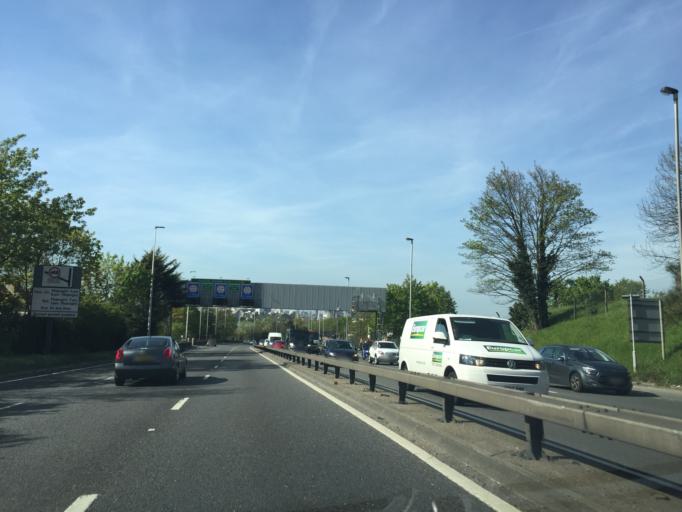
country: GB
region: England
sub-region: Greater London
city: Blackheath
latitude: 51.4801
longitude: 0.0217
